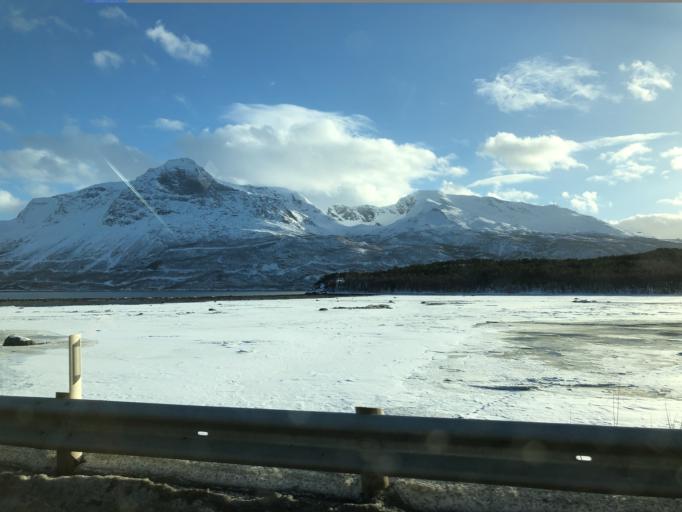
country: NO
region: Nordland
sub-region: Narvik
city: Bjerkvik
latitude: 68.4802
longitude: 17.5476
